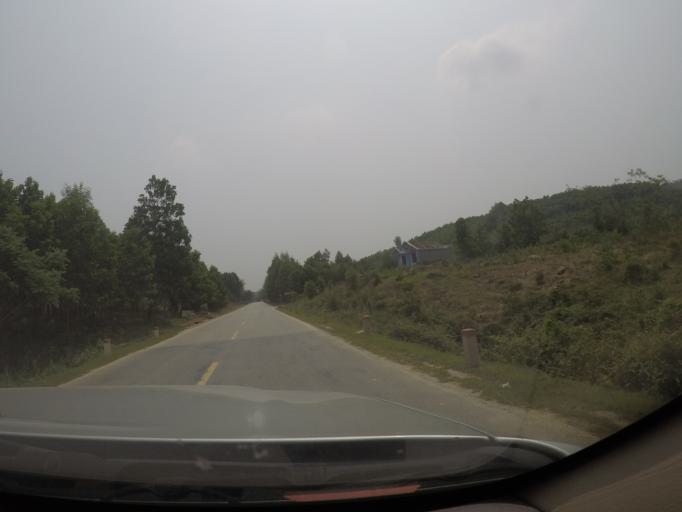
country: VN
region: Thanh Hoa
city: Thi Tran Yen Cat
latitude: 19.7461
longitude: 105.4231
